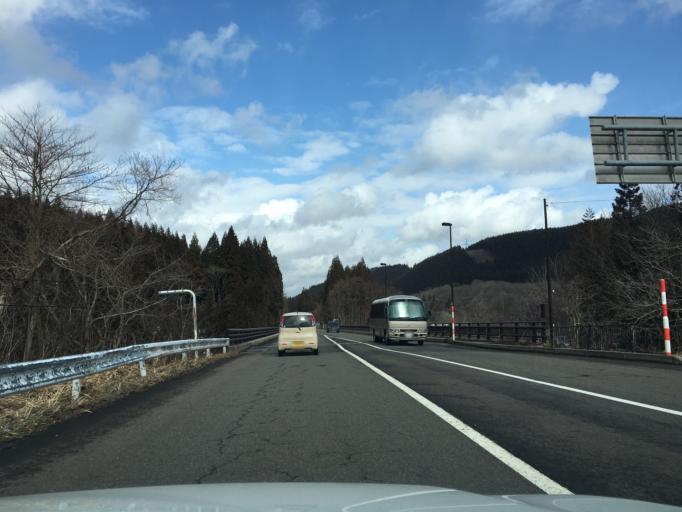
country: JP
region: Akita
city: Takanosu
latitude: 40.0087
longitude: 140.2786
